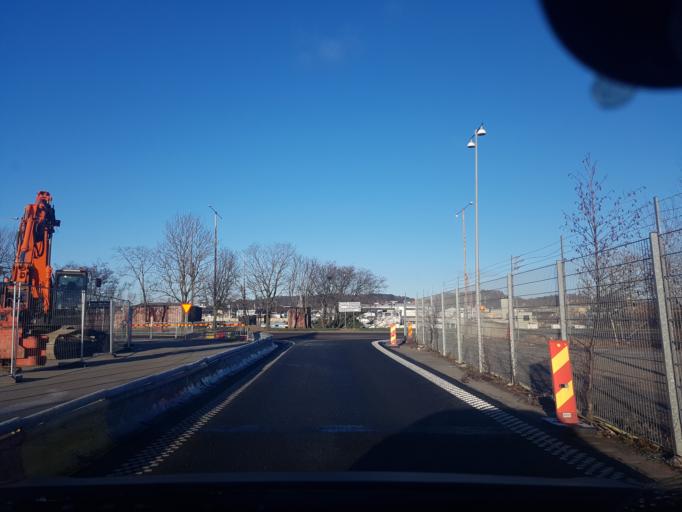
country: SE
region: Vaestra Goetaland
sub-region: Goteborg
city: Goeteborg
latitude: 57.7184
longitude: 11.9828
